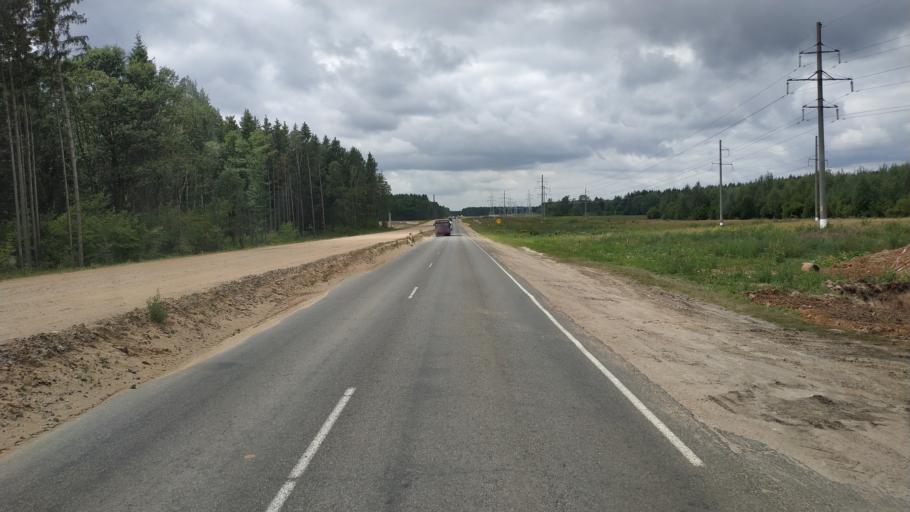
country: BY
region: Mogilev
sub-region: Mahilyowski Rayon
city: Kadino
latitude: 53.8717
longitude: 30.4534
